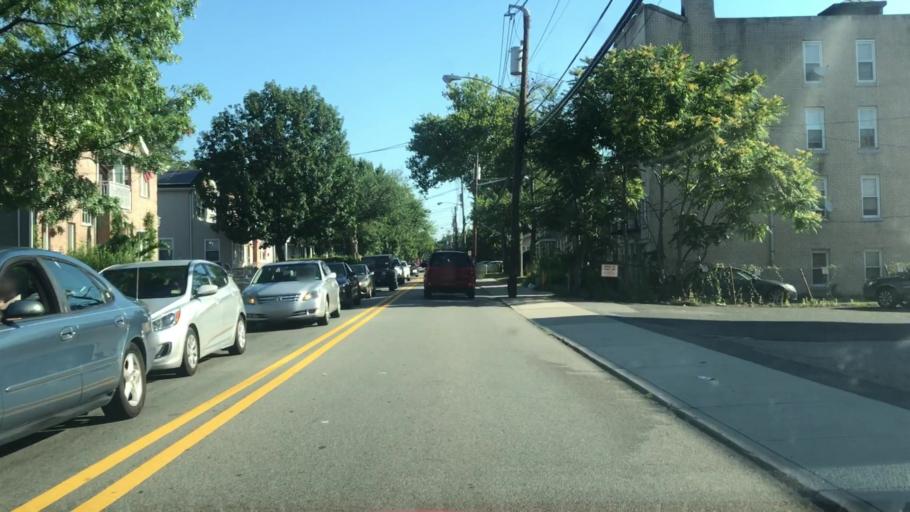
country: US
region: New Jersey
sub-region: Bergen County
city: Ridgefield Park
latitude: 40.8431
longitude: -74.0223
